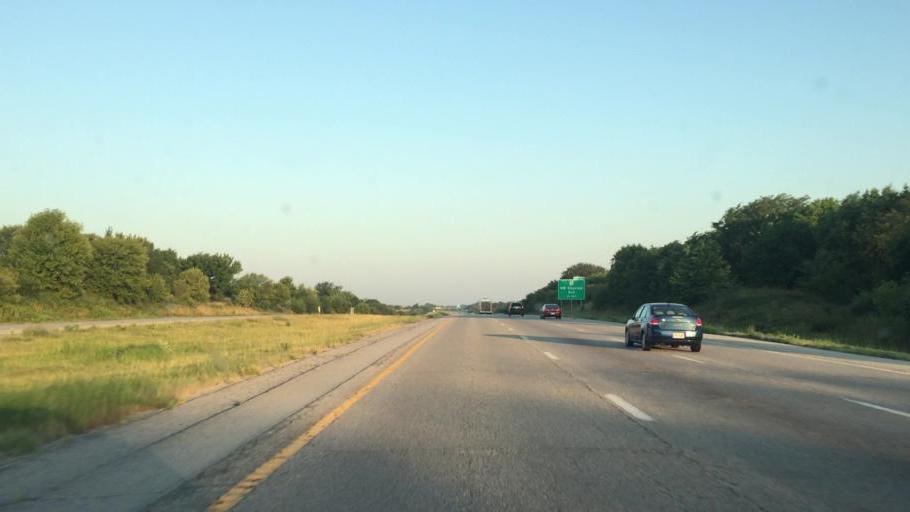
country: US
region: Missouri
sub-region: Platte County
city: Weatherby Lake
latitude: 39.3075
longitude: -94.6334
